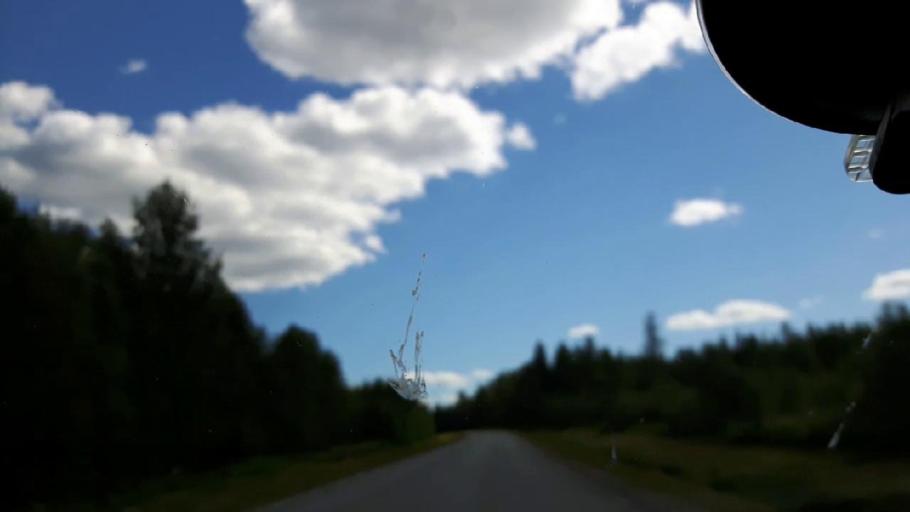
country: SE
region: Jaemtland
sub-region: Ragunda Kommun
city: Hammarstrand
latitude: 62.8282
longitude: 16.1864
